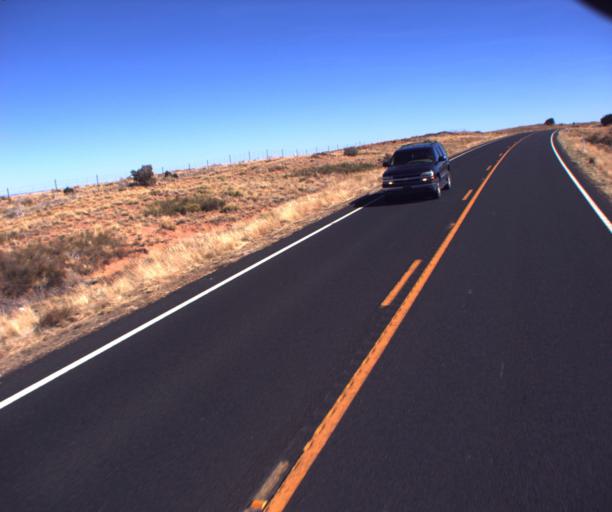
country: US
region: Arizona
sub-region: Apache County
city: Ganado
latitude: 35.7875
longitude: -109.6746
